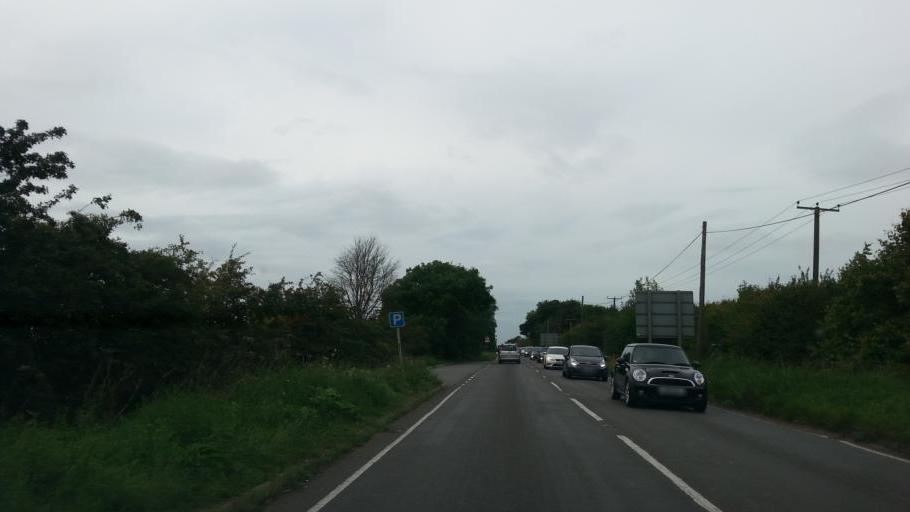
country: GB
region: England
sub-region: Cambridgeshire
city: Papworth Everard
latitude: 52.2297
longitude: -0.1039
